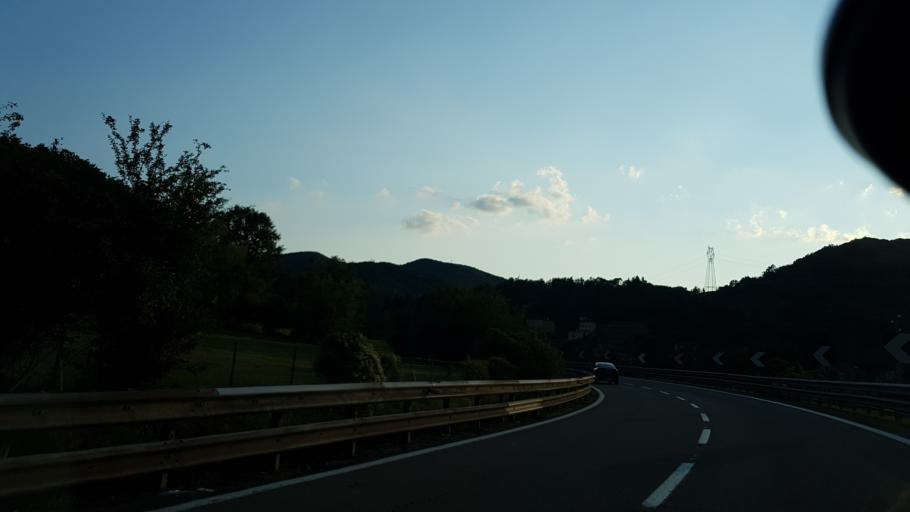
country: IT
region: Liguria
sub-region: Provincia di Genova
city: Borgo Fornari-Pieve
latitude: 44.5939
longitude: 8.9427
